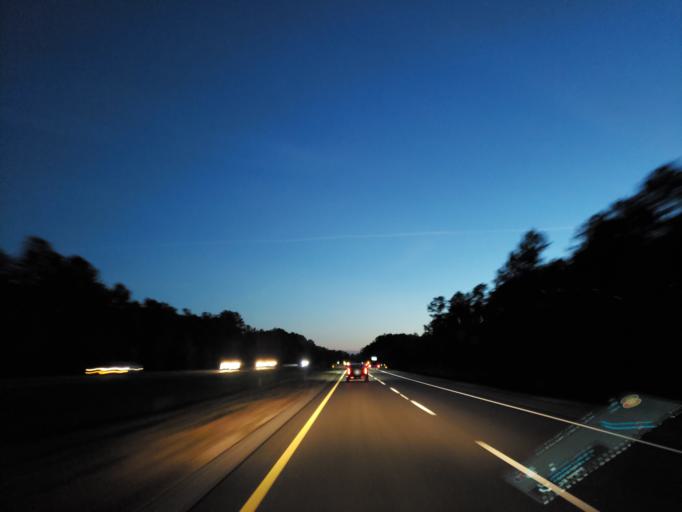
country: US
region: Mississippi
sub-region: Clarke County
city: Stonewall
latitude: 32.2298
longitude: -88.8325
